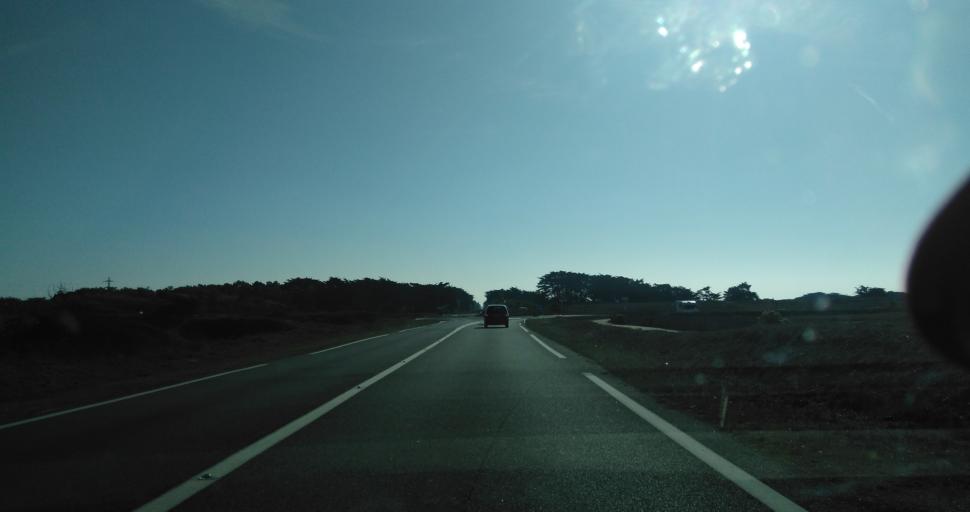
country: FR
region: Brittany
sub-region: Departement du Morbihan
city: Plouharnel
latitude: 47.5778
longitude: -3.1348
